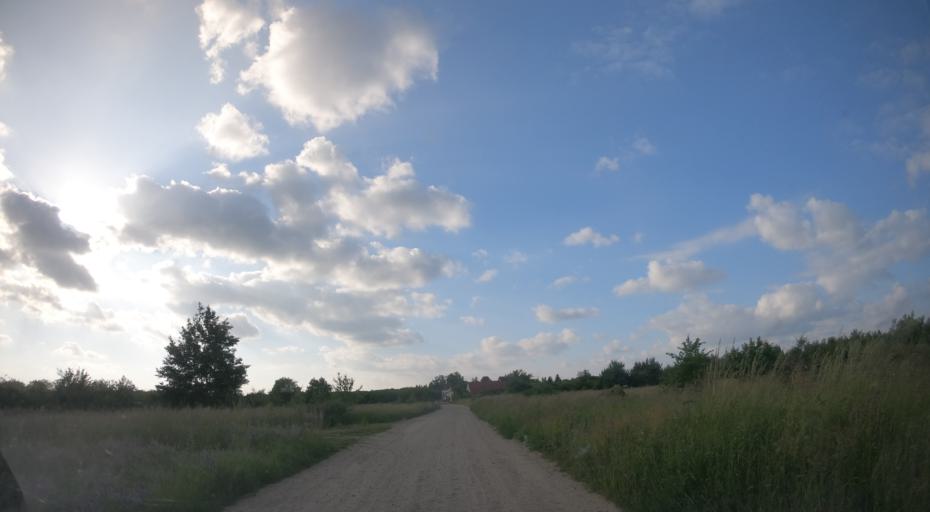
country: PL
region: Lubusz
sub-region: Powiat gorzowski
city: Santok
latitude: 52.7415
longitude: 15.3968
